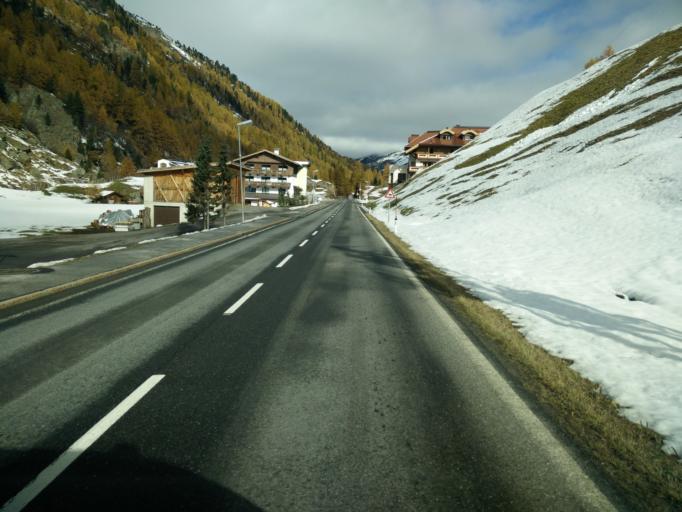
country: AT
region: Tyrol
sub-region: Politischer Bezirk Imst
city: Soelden
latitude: 46.8989
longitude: 11.0401
